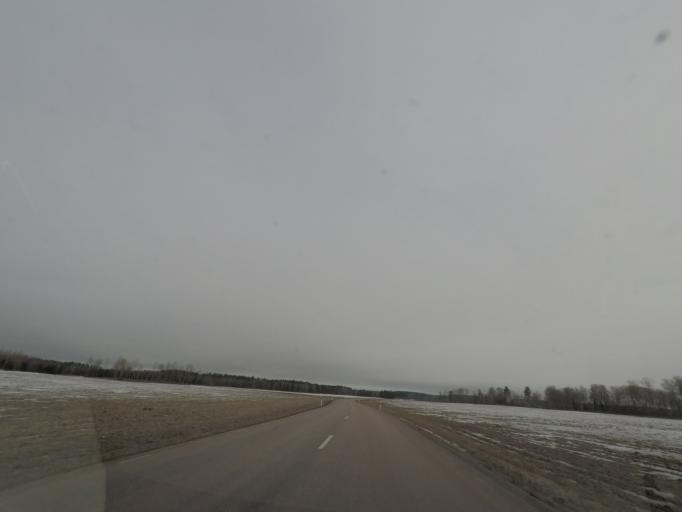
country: SE
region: Vaestmanland
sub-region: Vasteras
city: Skultuna
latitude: 59.7337
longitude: 16.4139
